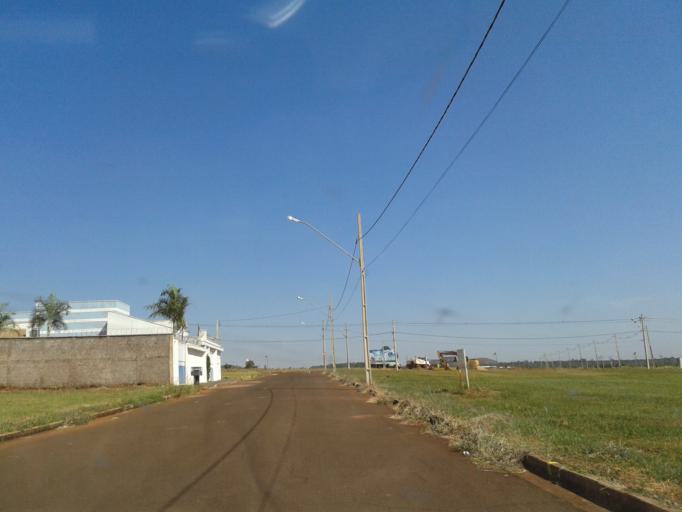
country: BR
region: Minas Gerais
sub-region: Ituiutaba
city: Ituiutaba
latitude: -19.0012
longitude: -49.4648
